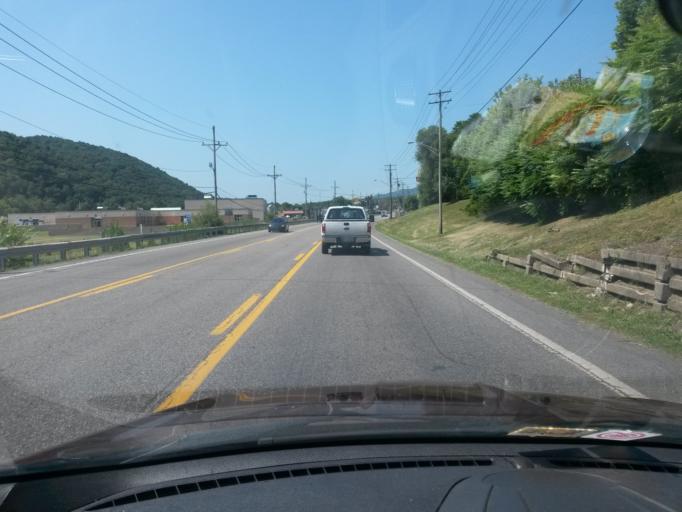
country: US
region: West Virginia
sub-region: Mineral County
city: Keyser
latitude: 39.4310
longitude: -78.9874
